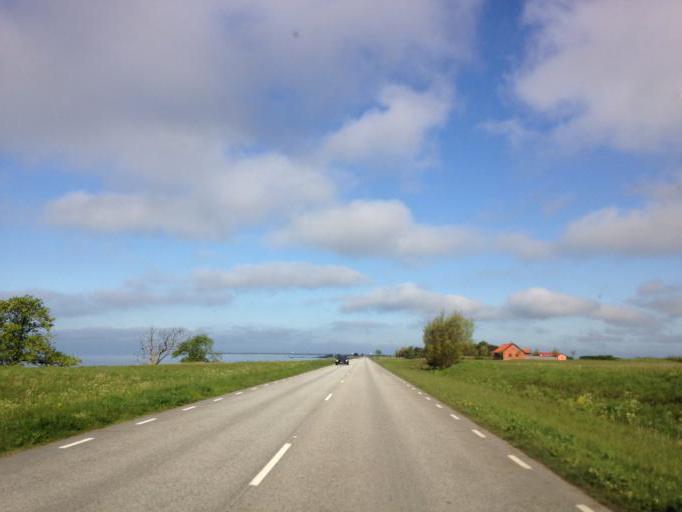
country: SE
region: Skane
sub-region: Trelleborgs Kommun
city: Skare
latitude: 55.3796
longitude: 13.0422
